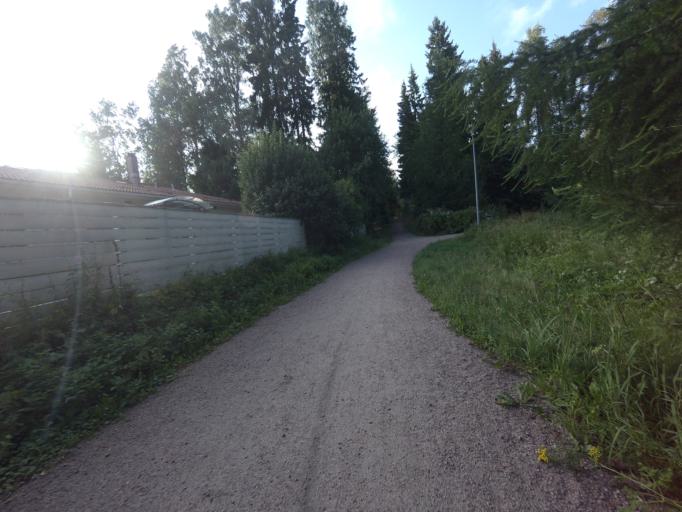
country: FI
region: Uusimaa
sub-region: Helsinki
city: Espoo
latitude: 60.1599
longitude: 24.6690
